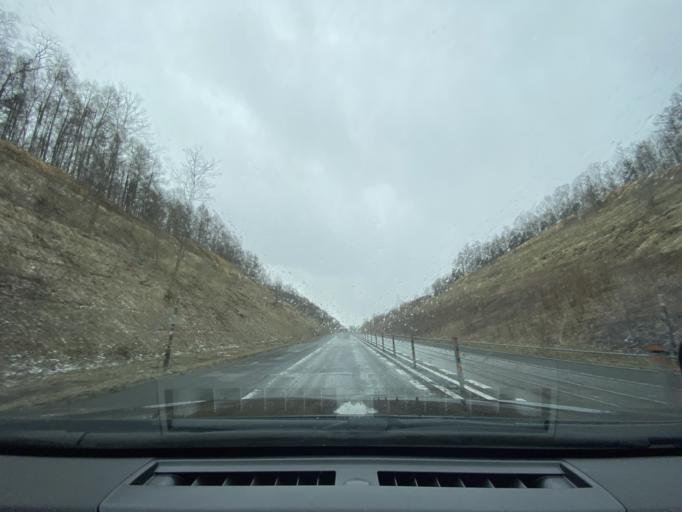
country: JP
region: Hokkaido
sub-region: Asahikawa-shi
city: Asahikawa
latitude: 43.8809
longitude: 142.4523
